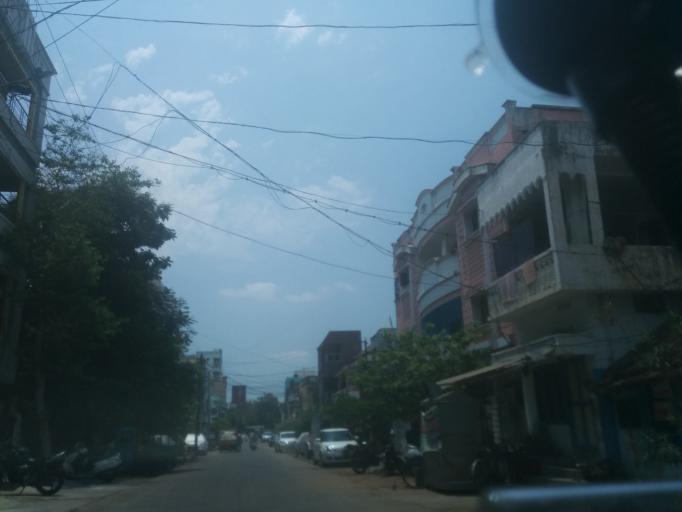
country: IN
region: Andhra Pradesh
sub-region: East Godavari
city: Rajahmundry
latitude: 16.9943
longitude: 81.7725
